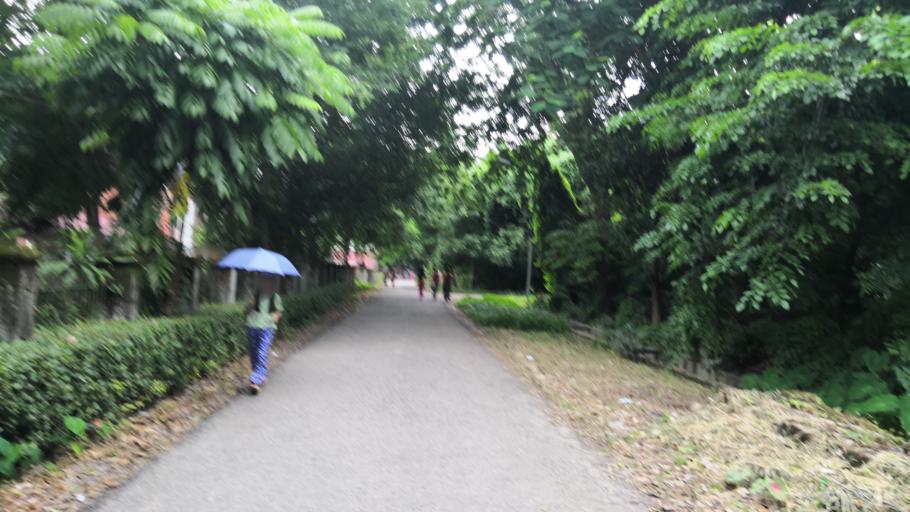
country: MM
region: Yangon
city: Yangon
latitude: 16.8299
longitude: 96.1335
